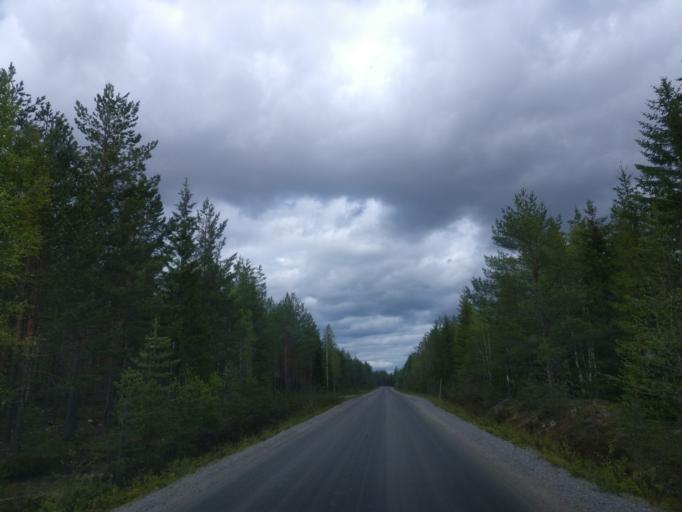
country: SE
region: Gaevleborg
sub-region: Soderhamns Kommun
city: Soderhamn
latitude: 61.4315
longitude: 17.0006
